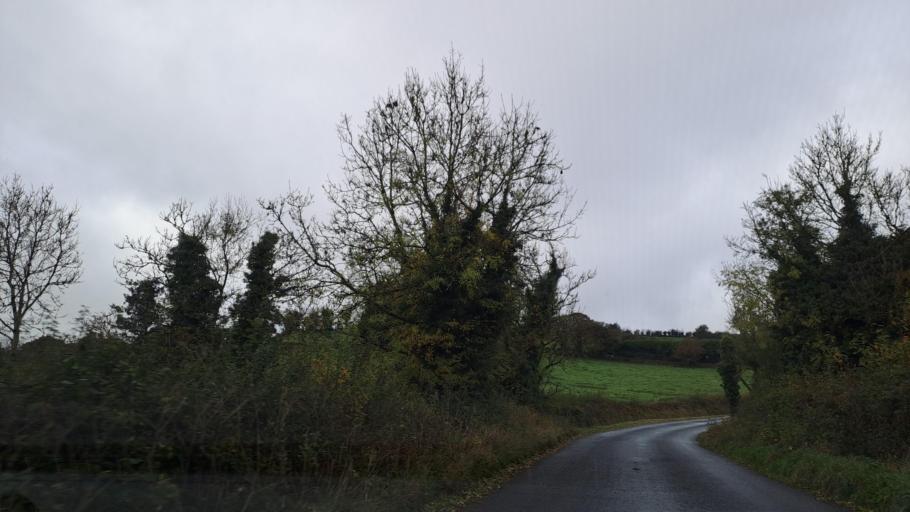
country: IE
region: Ulster
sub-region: An Cabhan
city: Bailieborough
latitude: 53.9925
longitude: -6.9418
